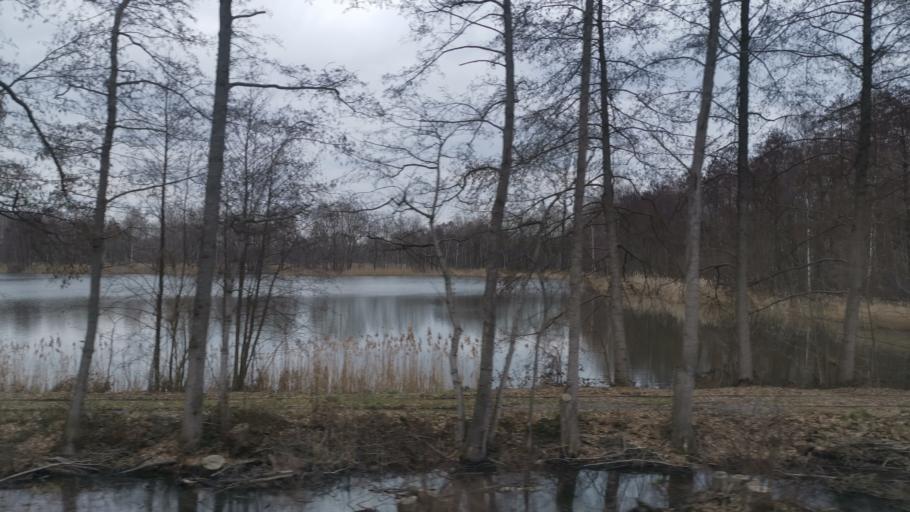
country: DE
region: Brandenburg
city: Ruckersdorf
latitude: 51.5987
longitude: 13.5670
